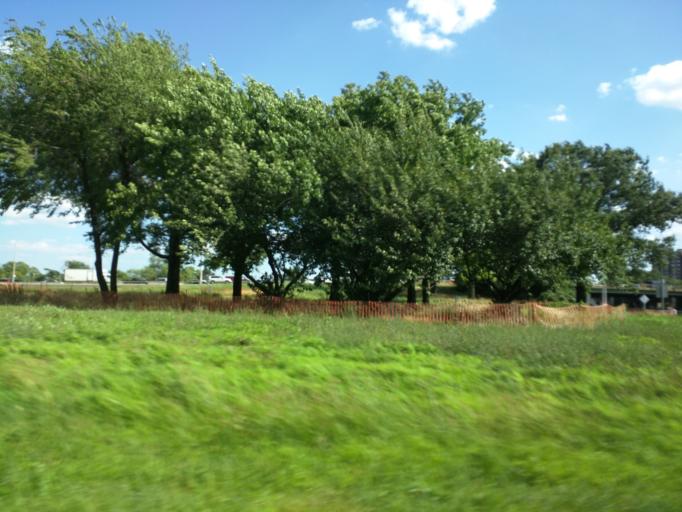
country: US
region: New York
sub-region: Queens County
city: Borough of Queens
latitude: 40.7416
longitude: -73.8451
